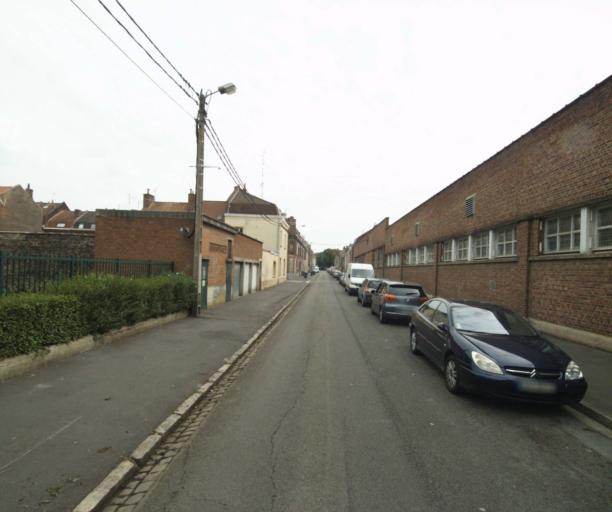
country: FR
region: Nord-Pas-de-Calais
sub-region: Departement du Nord
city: Loos
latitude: 50.6119
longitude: 3.0157
